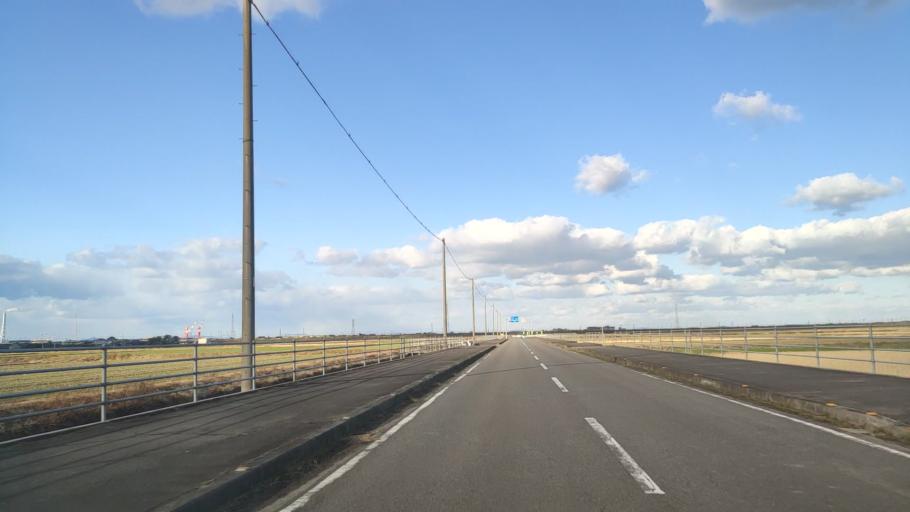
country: JP
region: Ehime
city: Saijo
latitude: 33.9008
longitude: 133.1354
